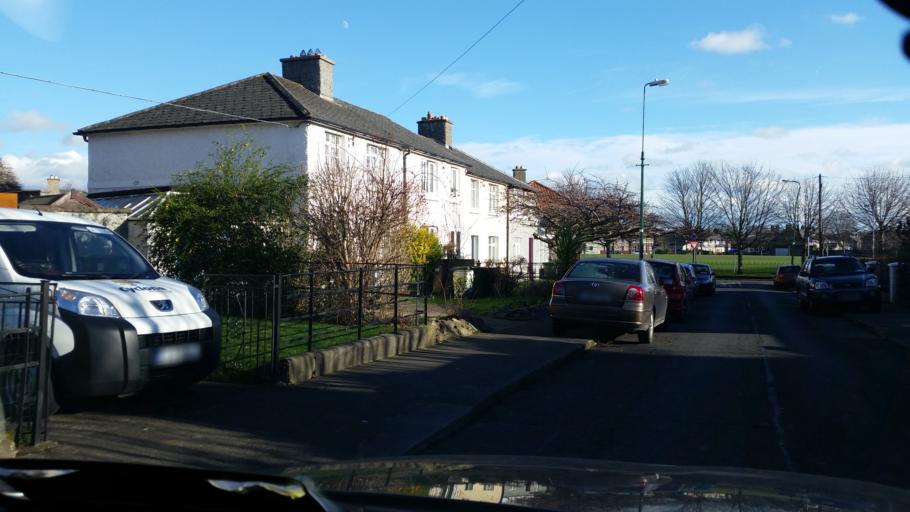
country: IE
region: Leinster
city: Marino
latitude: 53.3671
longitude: -6.2360
